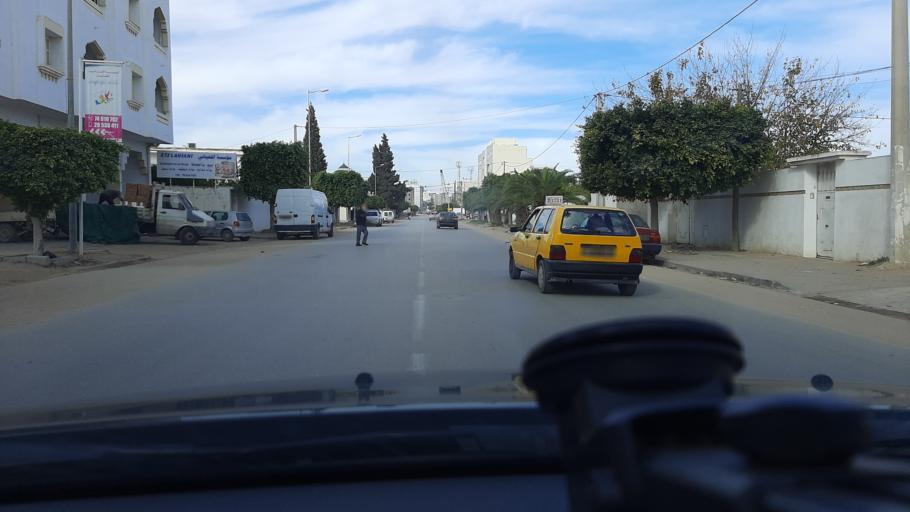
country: TN
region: Safaqis
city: Sfax
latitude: 34.7541
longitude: 10.7374
